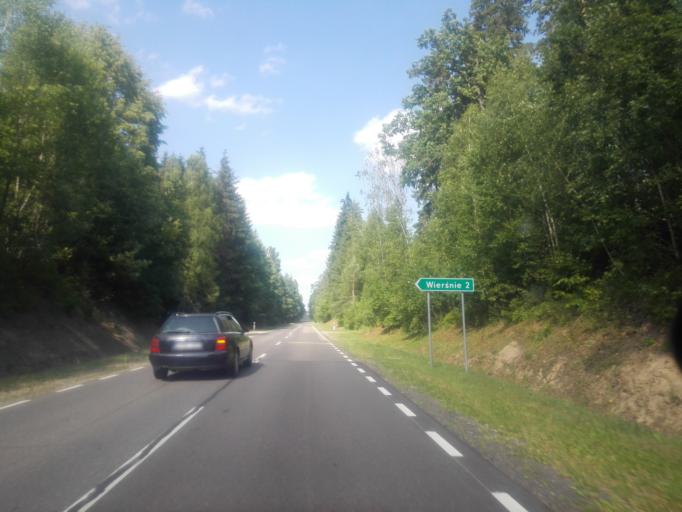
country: PL
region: Podlasie
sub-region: Powiat sejnenski
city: Sejny
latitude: 54.0161
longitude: 23.3353
